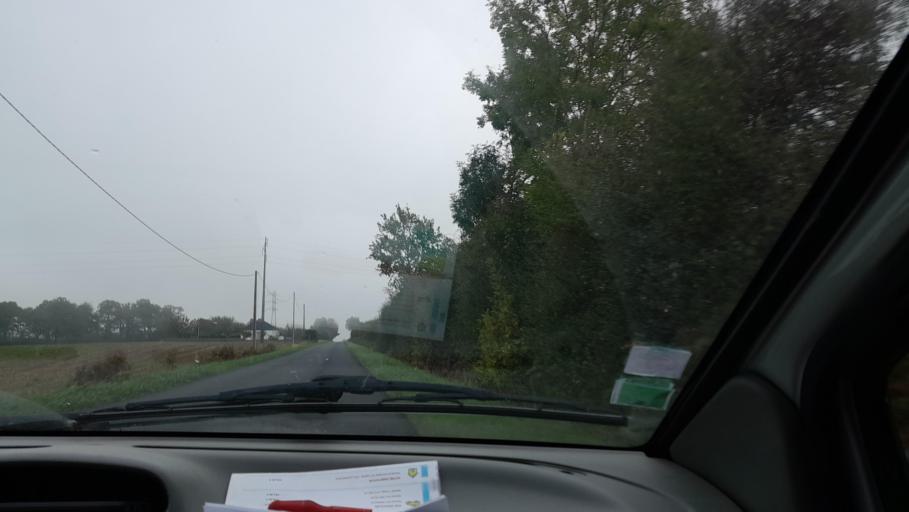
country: FR
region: Pays de la Loire
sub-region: Departement de la Mayenne
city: Saint-Pierre-la-Cour
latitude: 48.1230
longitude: -1.0249
